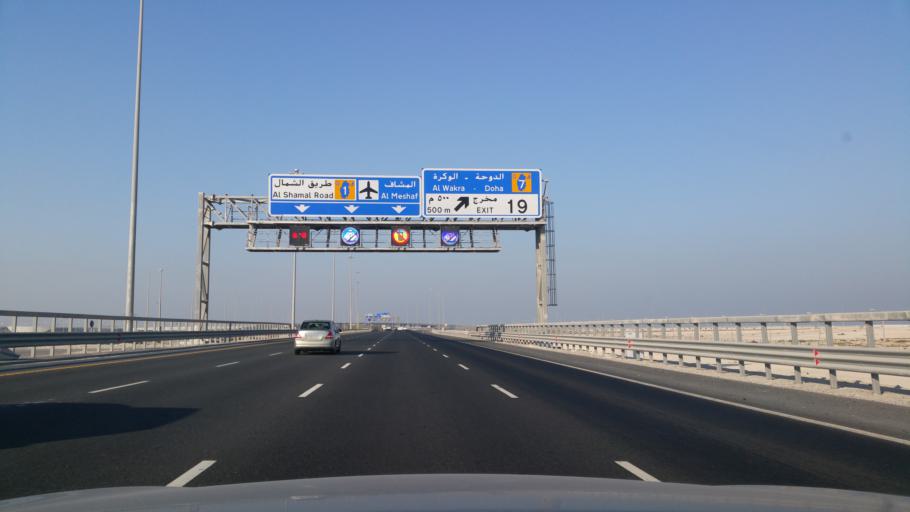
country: QA
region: Al Wakrah
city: Al Wukayr
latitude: 25.1126
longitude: 51.5849
